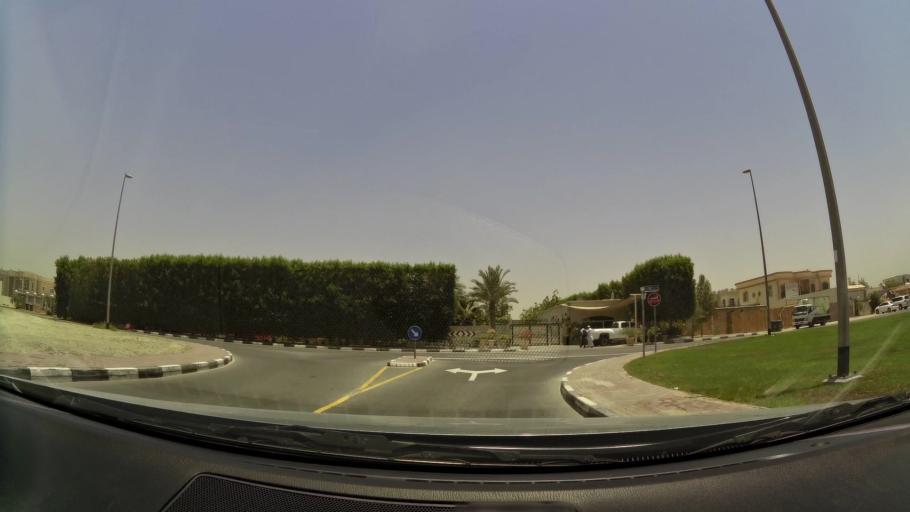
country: AE
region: Dubai
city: Dubai
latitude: 25.0973
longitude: 55.1863
